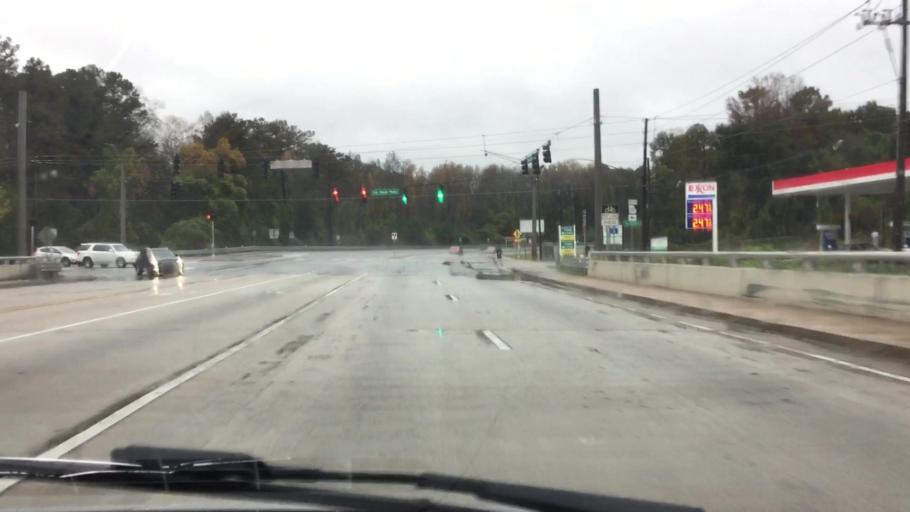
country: US
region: Georgia
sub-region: DeKalb County
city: Panthersville
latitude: 33.6862
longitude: -84.2015
